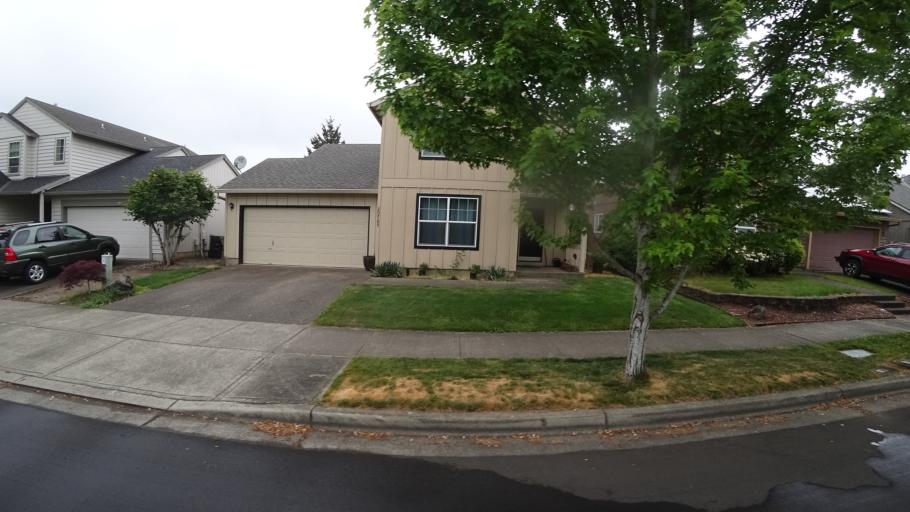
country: US
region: Oregon
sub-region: Washington County
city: Rockcreek
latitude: 45.5296
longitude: -122.8904
